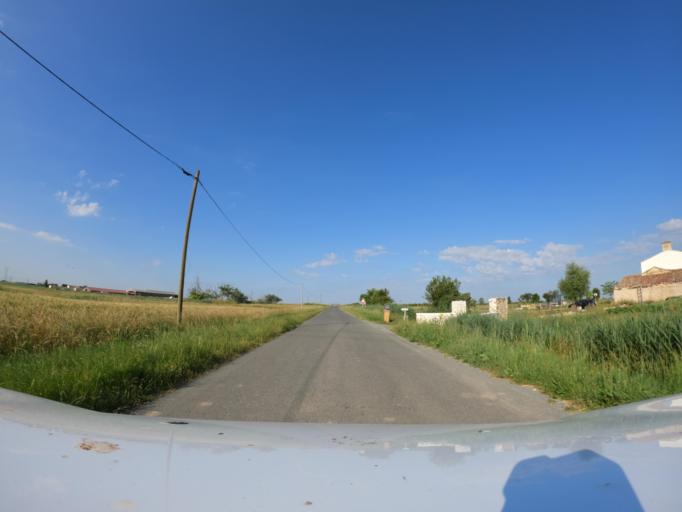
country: FR
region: Poitou-Charentes
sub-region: Departement de la Charente-Maritime
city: Charron
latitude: 46.3326
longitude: -1.1005
